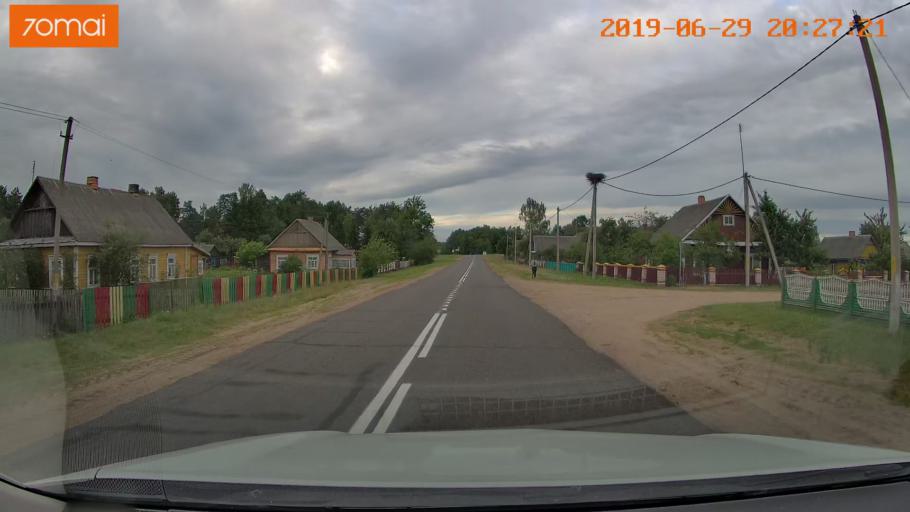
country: BY
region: Brest
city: Hantsavichy
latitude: 52.4731
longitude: 26.3037
